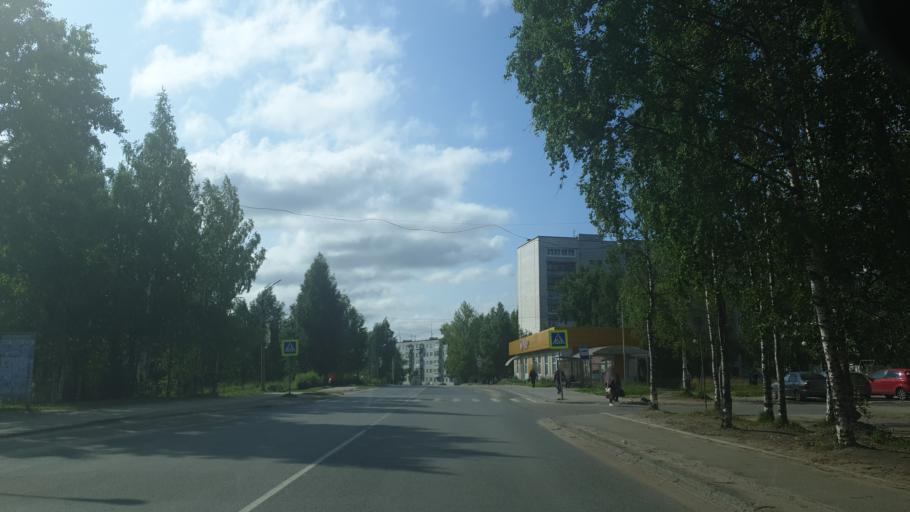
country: RU
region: Komi Republic
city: Ezhva
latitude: 61.7923
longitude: 50.7502
